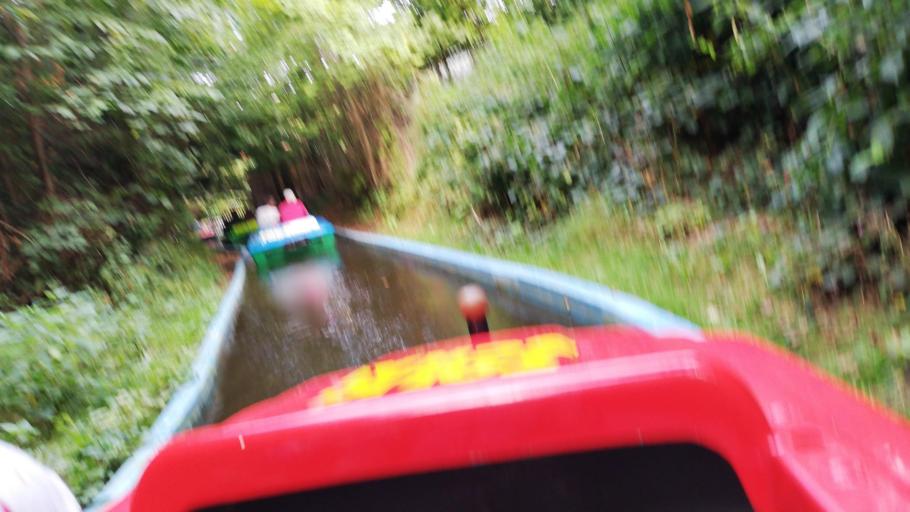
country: DE
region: Schleswig-Holstein
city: Tolk
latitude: 54.5772
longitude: 9.6243
